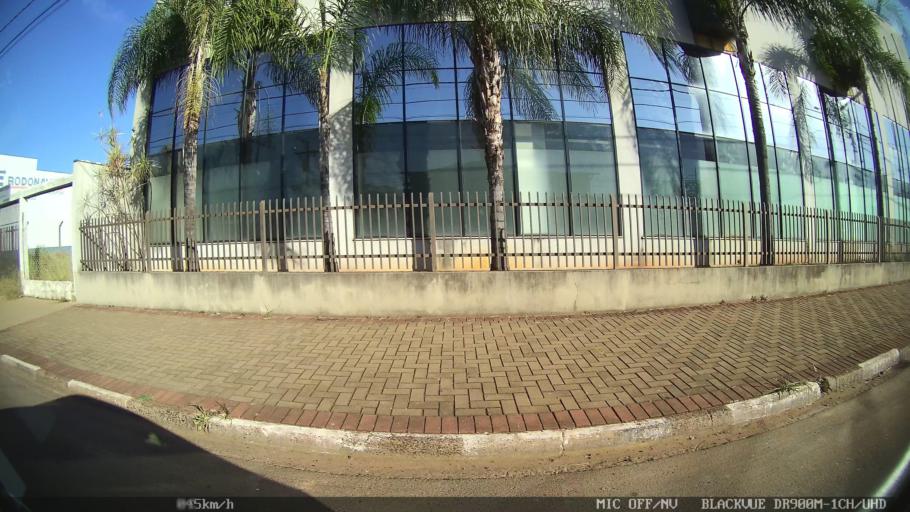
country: BR
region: Sao Paulo
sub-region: Franca
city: Franca
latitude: -20.5070
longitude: -47.3966
